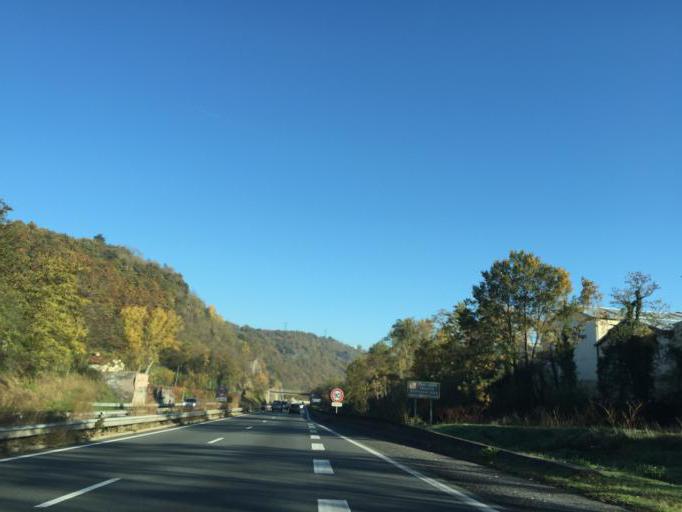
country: FR
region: Rhone-Alpes
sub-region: Departement de la Loire
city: Lorette
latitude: 45.5067
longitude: 4.5685
